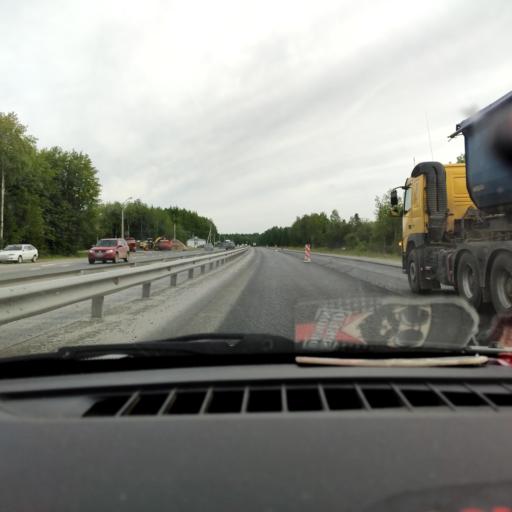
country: RU
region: Perm
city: Polazna
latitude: 58.2290
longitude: 56.4244
